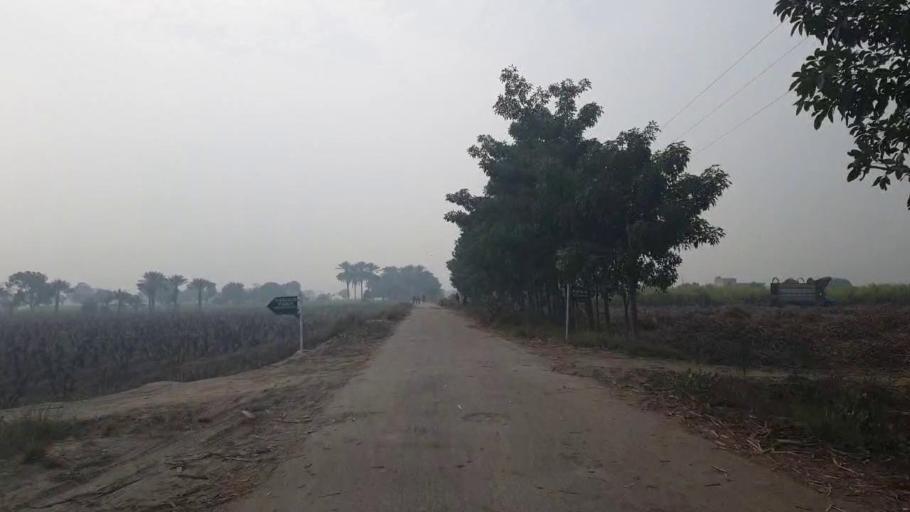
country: PK
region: Sindh
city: Tando Adam
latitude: 25.7172
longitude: 68.6804
